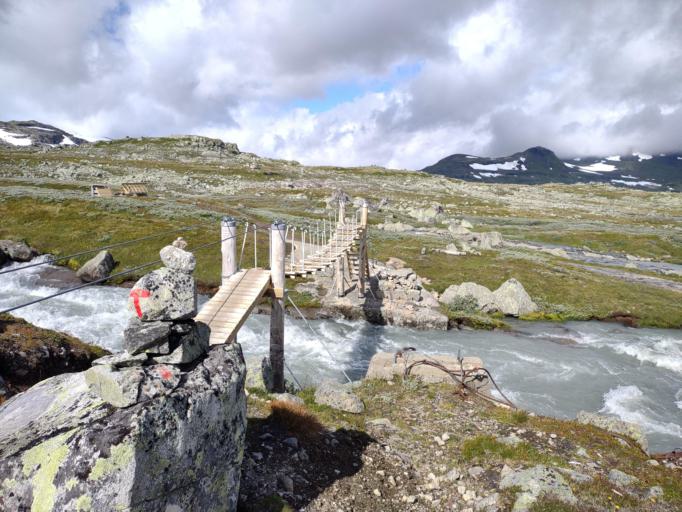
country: NO
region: Sogn og Fjordane
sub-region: Aurland
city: Aurlandsvangen
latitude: 60.5841
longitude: 7.5205
